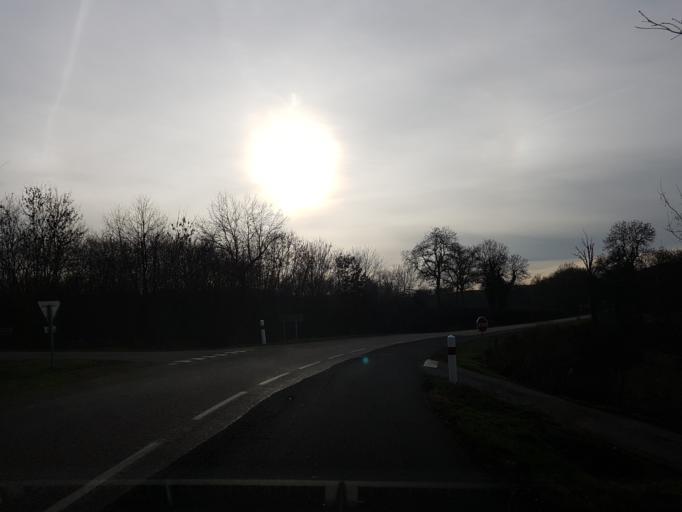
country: FR
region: Auvergne
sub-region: Departement de l'Allier
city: Souvigny
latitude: 46.4402
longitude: 3.0969
